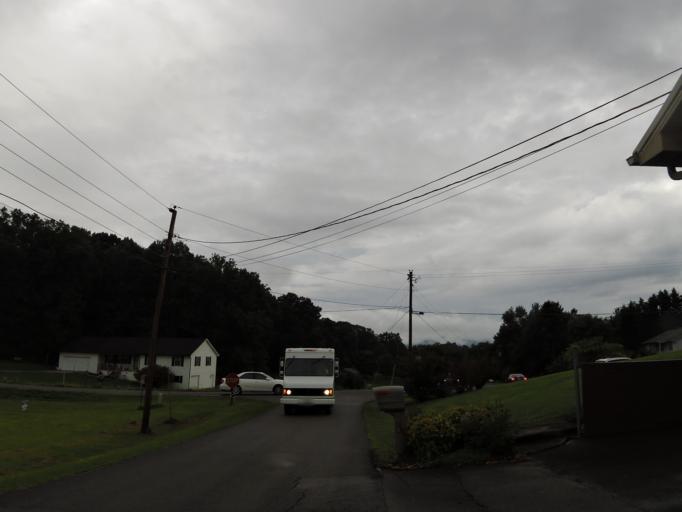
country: US
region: Tennessee
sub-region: Blount County
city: Wildwood
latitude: 35.7868
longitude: -83.8760
